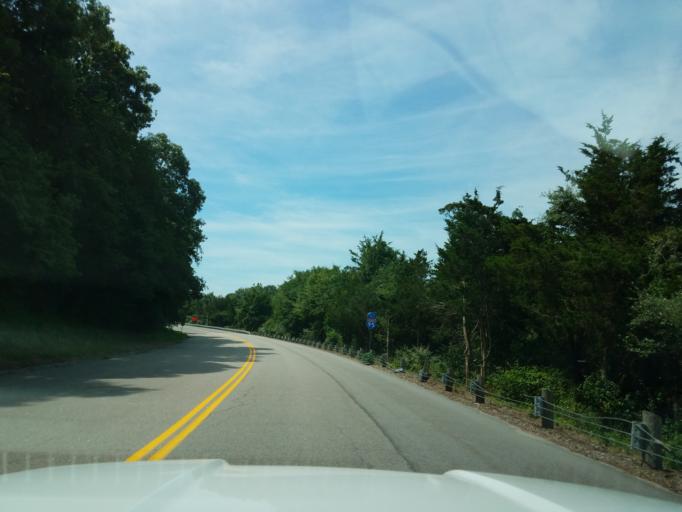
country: US
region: Connecticut
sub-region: New London County
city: Old Mystic
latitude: 41.3822
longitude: -71.9046
